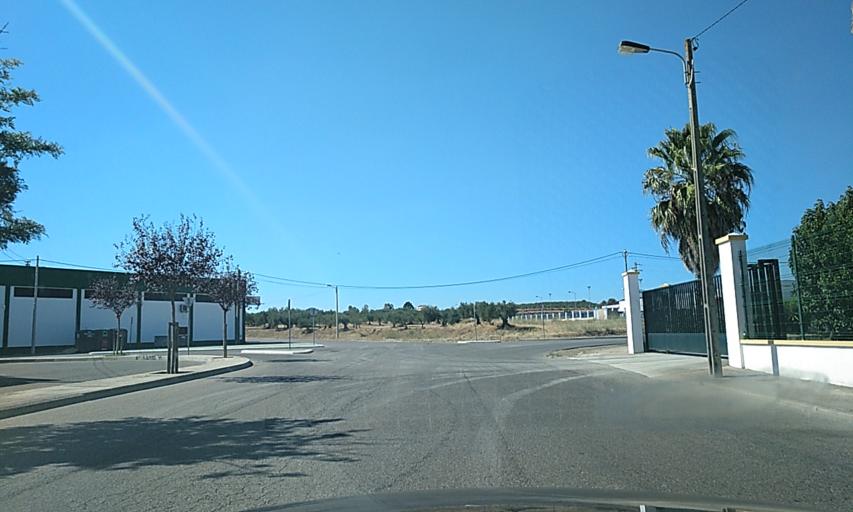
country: PT
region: Portalegre
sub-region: Campo Maior
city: Campo Maior
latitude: 39.0222
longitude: -7.0605
